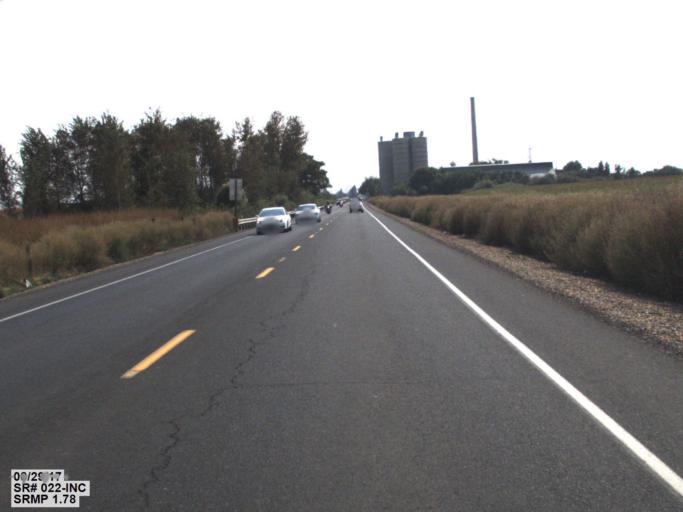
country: US
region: Washington
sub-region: Yakima County
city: Toppenish
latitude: 46.4011
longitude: -120.3146
